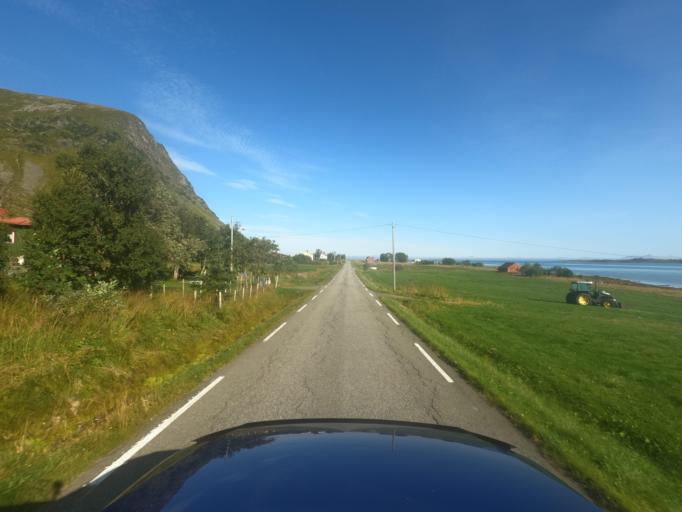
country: NO
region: Nordland
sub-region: Vestvagoy
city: Evjen
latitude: 68.3068
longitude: 14.0164
